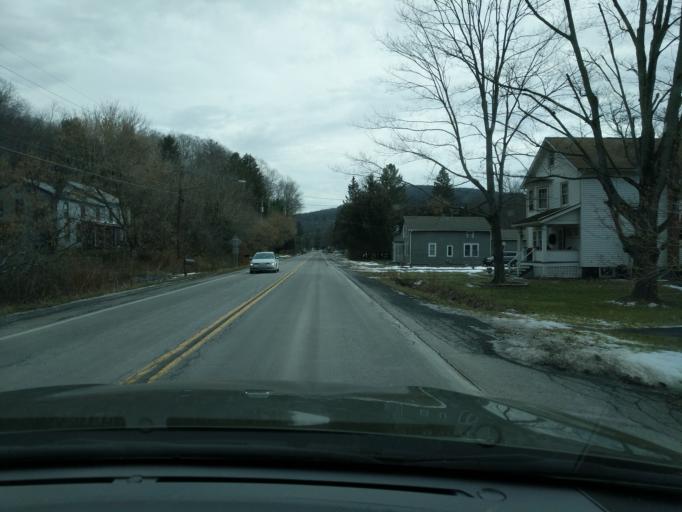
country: US
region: New York
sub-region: Tompkins County
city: East Ithaca
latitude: 42.3829
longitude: -76.4008
